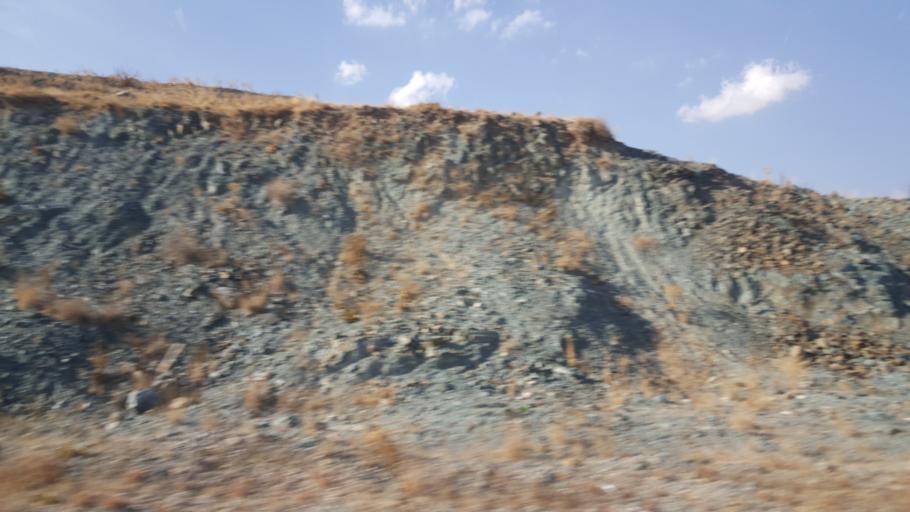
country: TR
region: Eskisehir
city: Kirka
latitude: 39.3287
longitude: 30.5773
